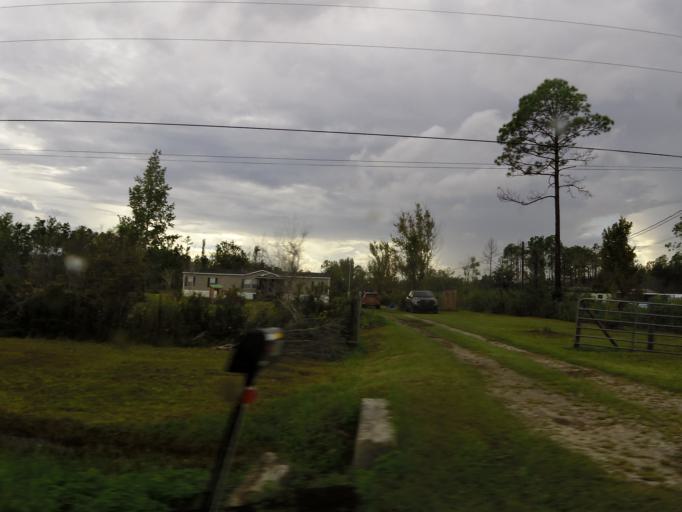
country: US
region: Florida
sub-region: Duval County
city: Baldwin
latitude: 30.4095
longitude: -82.0260
